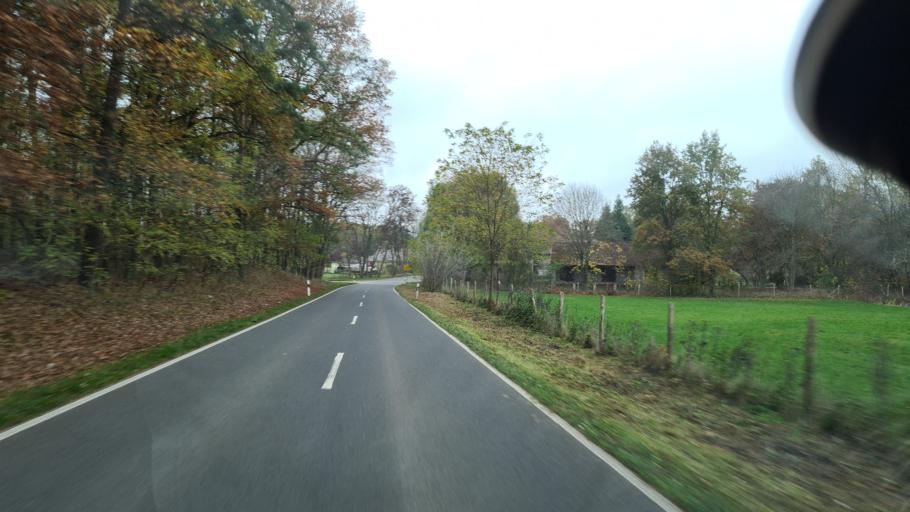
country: DE
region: Brandenburg
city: Lindow
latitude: 52.9617
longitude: 12.9955
